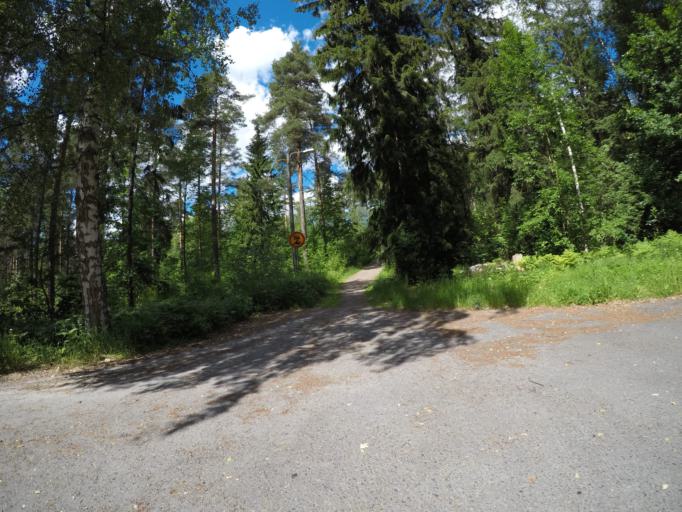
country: FI
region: Haeme
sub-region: Haemeenlinna
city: Haemeenlinna
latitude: 61.0128
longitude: 24.4340
